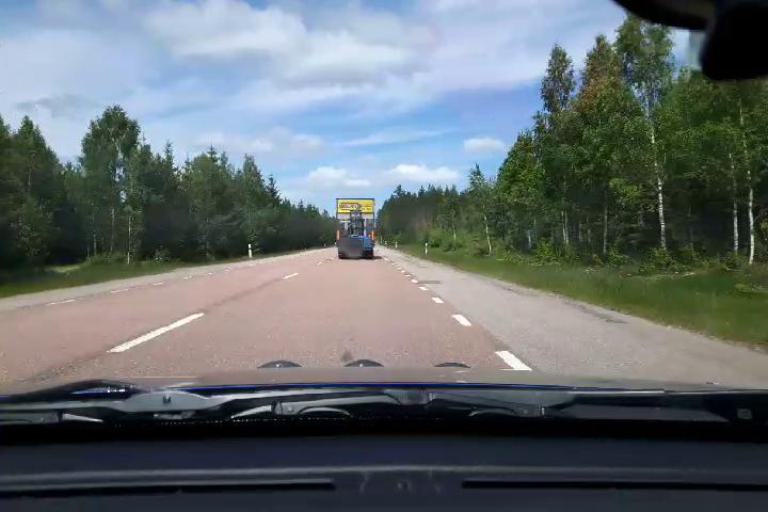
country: SE
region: Uppsala
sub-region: Osthammars Kommun
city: Bjorklinge
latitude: 60.1592
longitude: 17.4912
